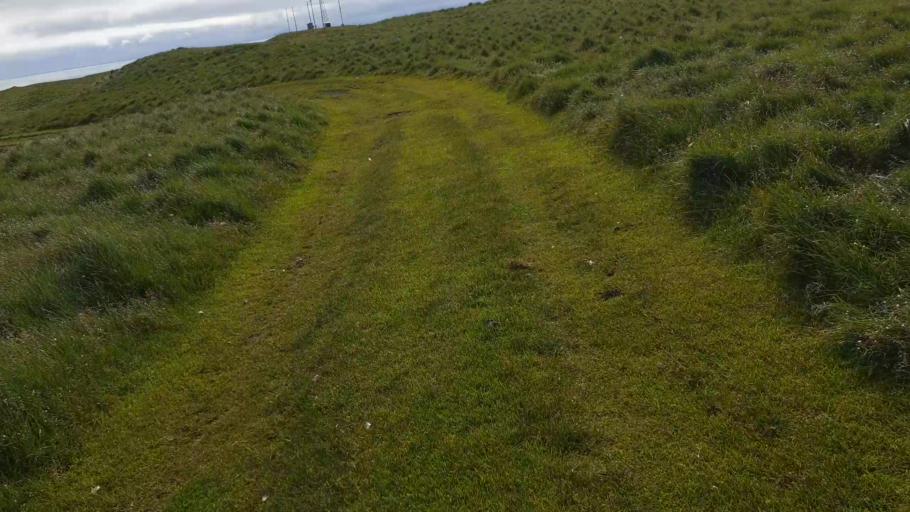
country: IS
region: Northeast
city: Dalvik
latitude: 66.5496
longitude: -17.9924
